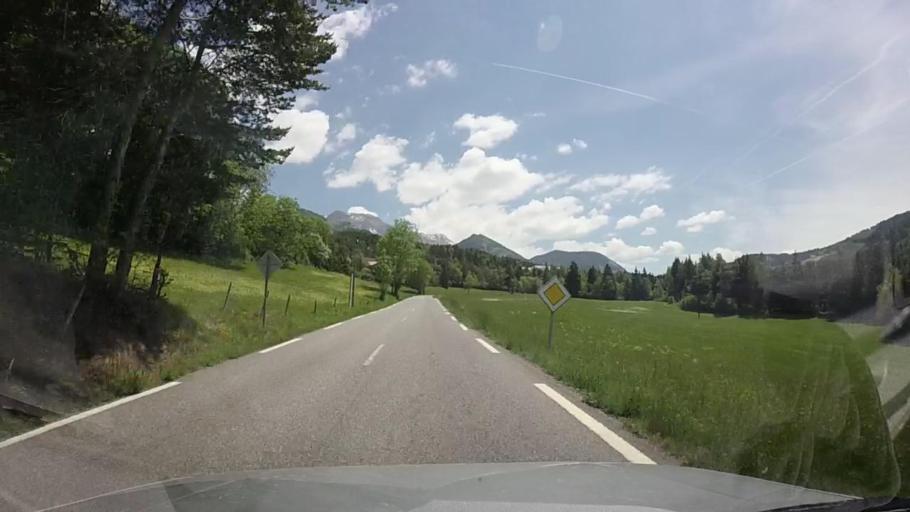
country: FR
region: Provence-Alpes-Cote d'Azur
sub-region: Departement des Alpes-de-Haute-Provence
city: Seyne-les-Alpes
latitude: 44.3344
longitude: 6.3878
